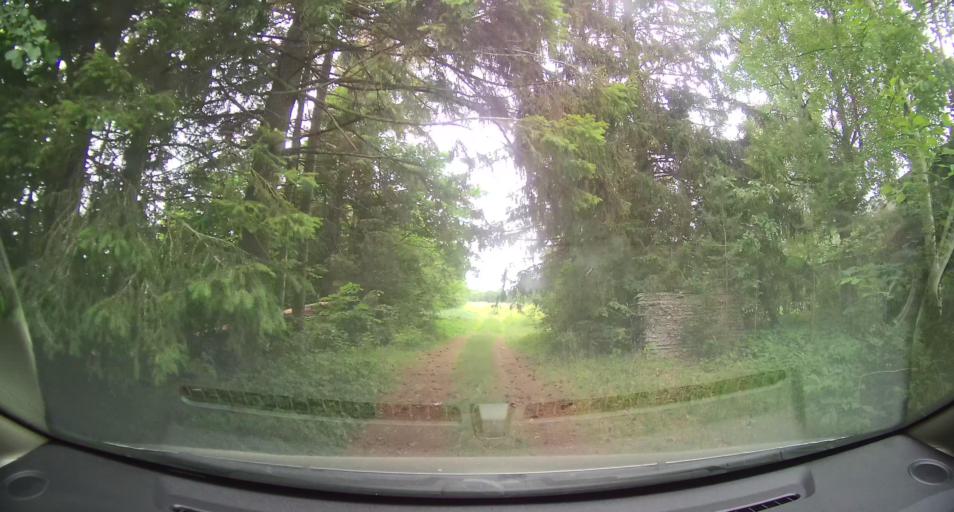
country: EE
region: Laeaene
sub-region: Lihula vald
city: Lihula
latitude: 58.5941
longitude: 23.7266
